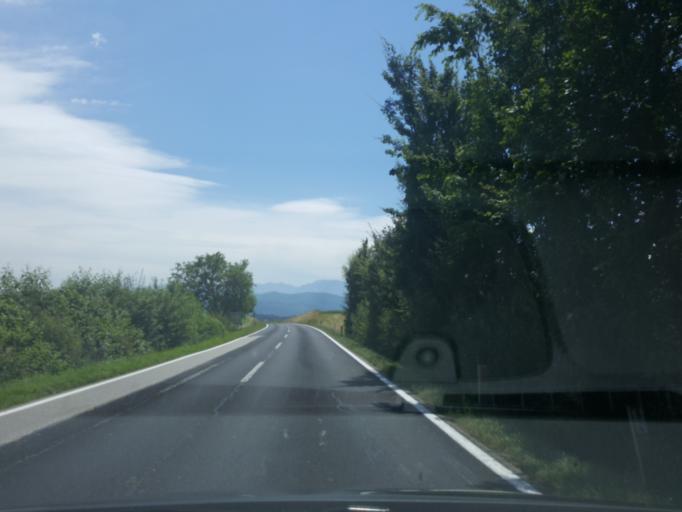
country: AT
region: Upper Austria
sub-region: Politischer Bezirk Vocklabruck
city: Gampern
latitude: 47.9757
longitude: 13.5618
